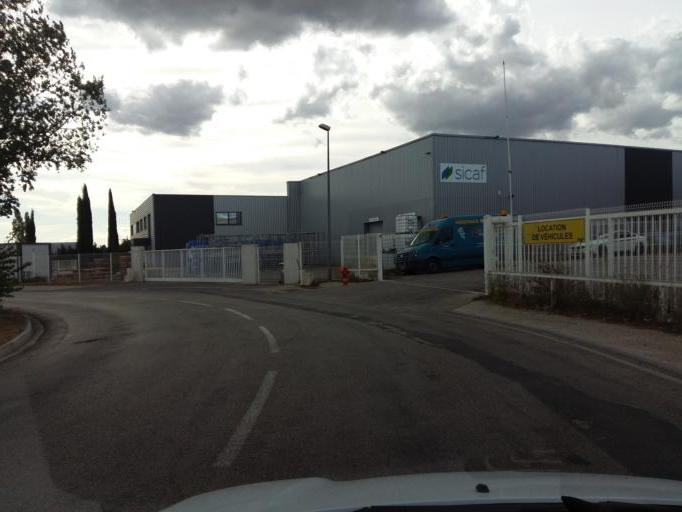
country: FR
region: Provence-Alpes-Cote d'Azur
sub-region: Departement du Vaucluse
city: Carpentras
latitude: 44.0380
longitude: 5.0373
